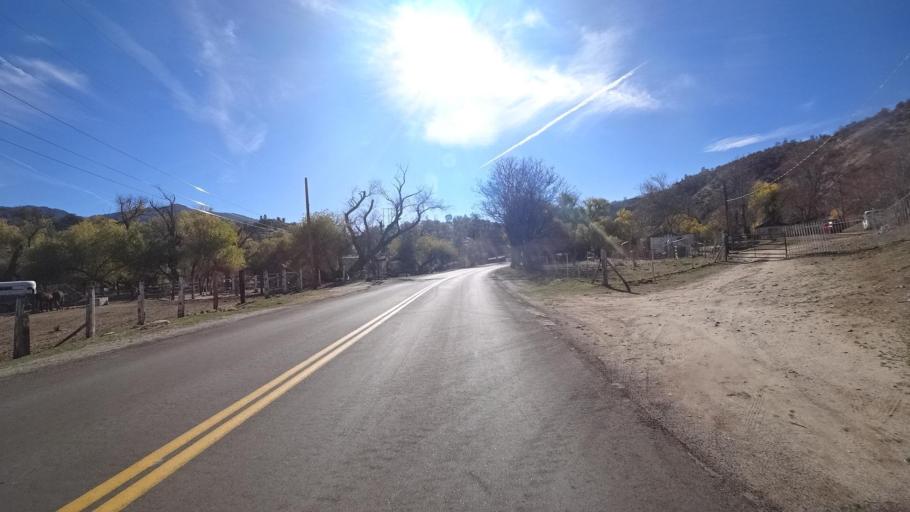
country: US
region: California
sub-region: Kern County
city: Bodfish
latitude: 35.5198
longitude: -118.5145
